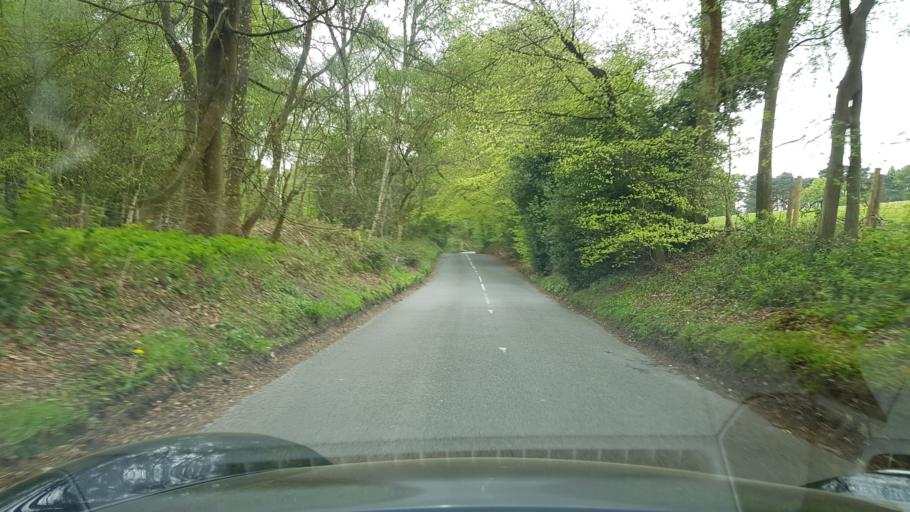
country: GB
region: England
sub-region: Surrey
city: East Horsley
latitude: 51.2427
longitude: -0.4421
